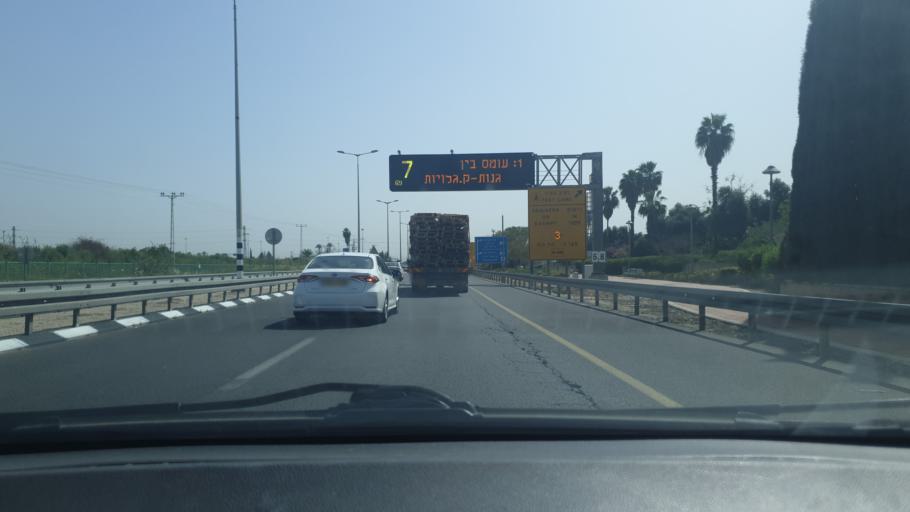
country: IL
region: Central District
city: Bet Dagan
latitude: 32.0053
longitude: 34.8296
